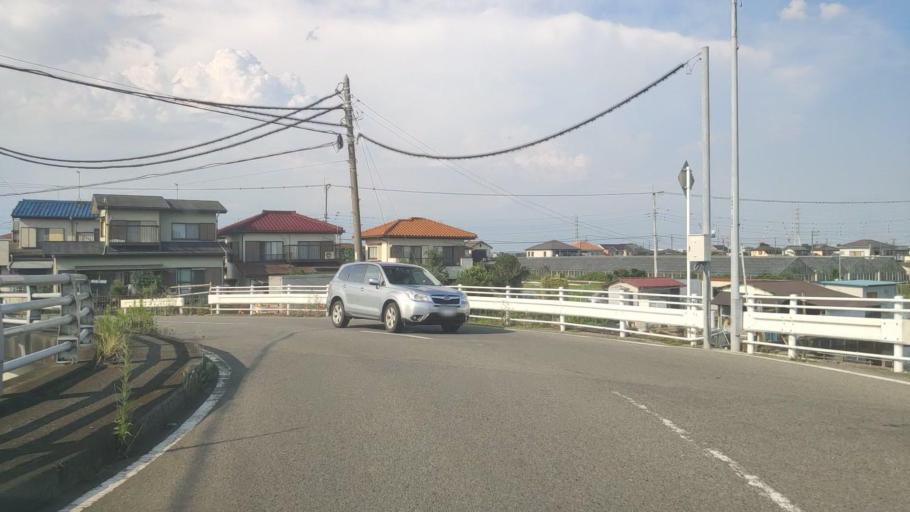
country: JP
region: Kanagawa
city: Isehara
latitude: 35.3836
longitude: 139.3390
